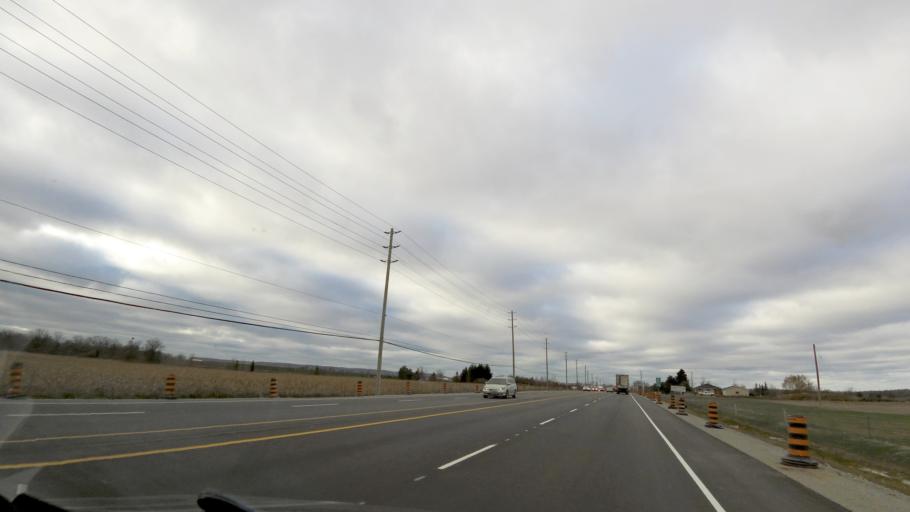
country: CA
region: Ontario
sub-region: Halton
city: Milton
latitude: 43.4735
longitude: -79.8163
